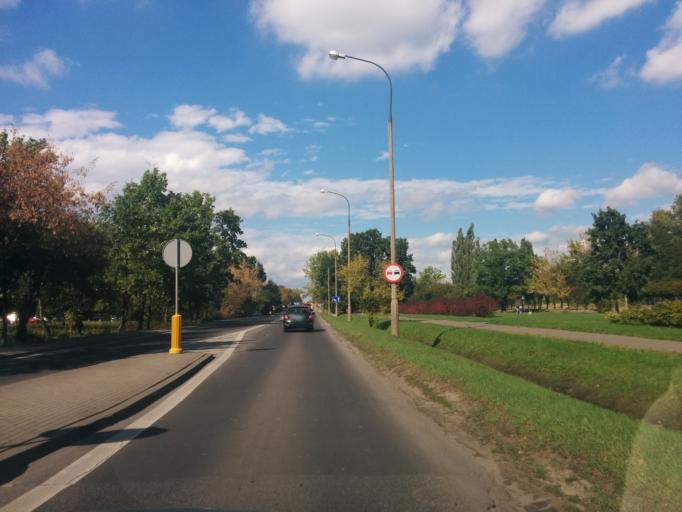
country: PL
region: Masovian Voivodeship
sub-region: Warszawa
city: Bialoleka
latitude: 52.3176
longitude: 20.9986
